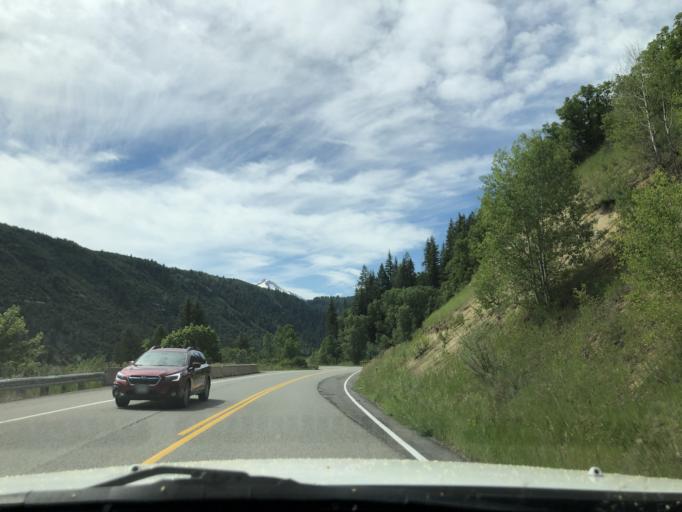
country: US
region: Colorado
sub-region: Delta County
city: Paonia
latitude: 38.9739
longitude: -107.3419
